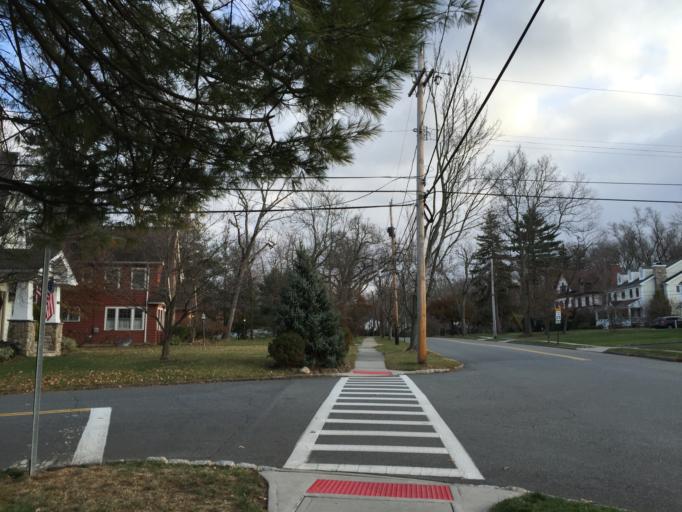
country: US
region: New Jersey
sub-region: Morris County
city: Chatham
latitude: 40.7205
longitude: -74.3740
